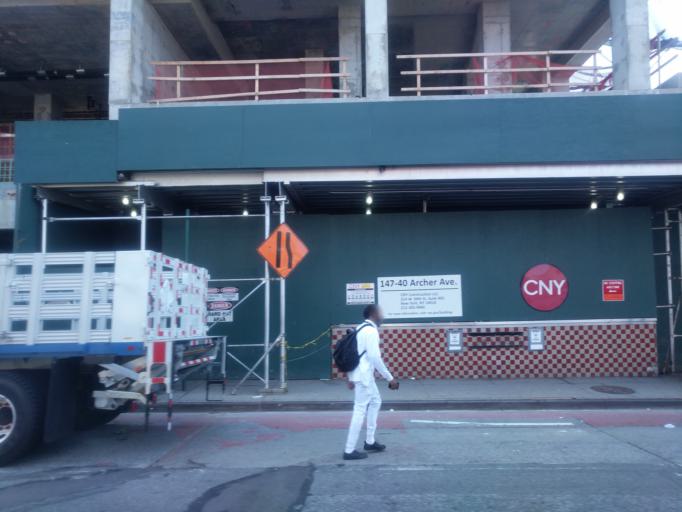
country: US
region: New York
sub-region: Queens County
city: Jamaica
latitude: 40.7005
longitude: -73.8072
